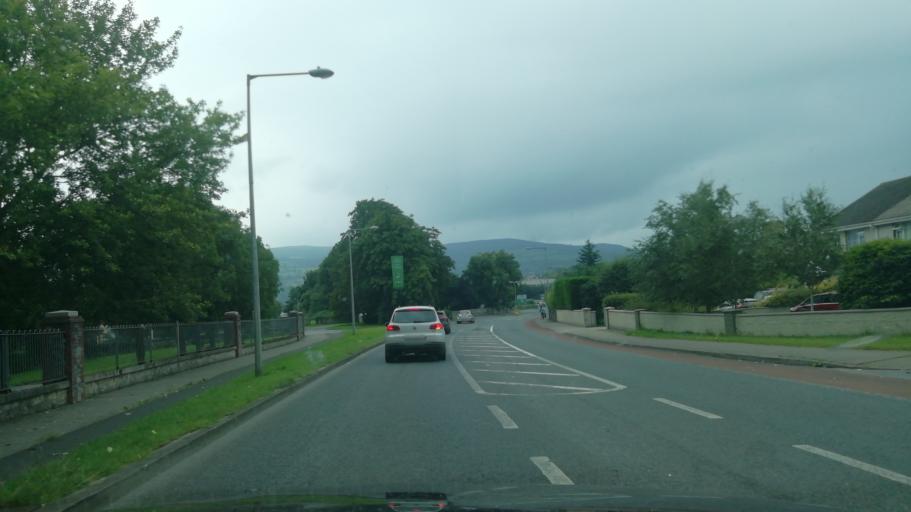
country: IE
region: Munster
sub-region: South Tipperary
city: Cluain Meala
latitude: 52.3656
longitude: -7.6995
